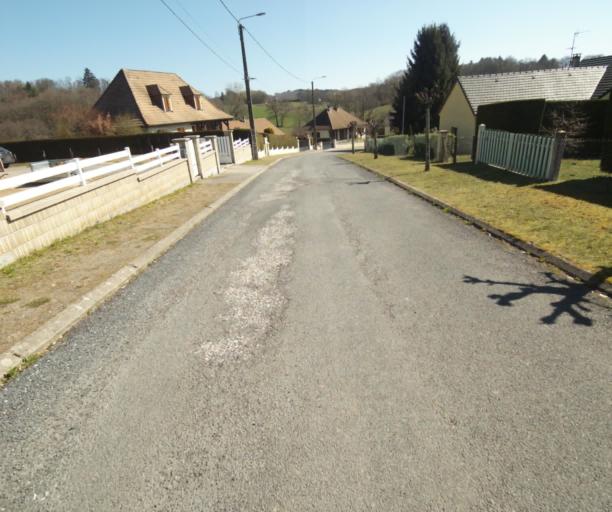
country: FR
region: Limousin
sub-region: Departement de la Correze
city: Saint-Mexant
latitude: 45.3119
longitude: 1.6476
